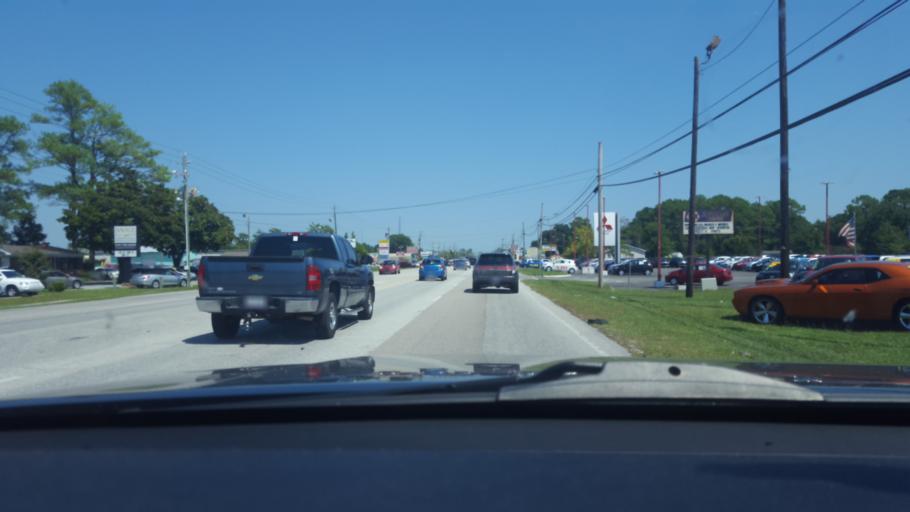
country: US
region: North Carolina
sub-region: New Hanover County
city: Kings Grant
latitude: 34.2532
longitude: -77.8496
